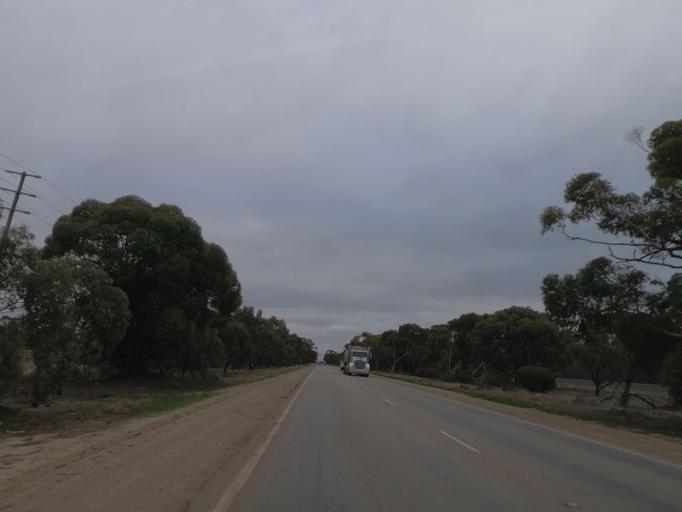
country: AU
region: Victoria
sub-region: Swan Hill
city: Swan Hill
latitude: -35.4034
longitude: 143.5794
